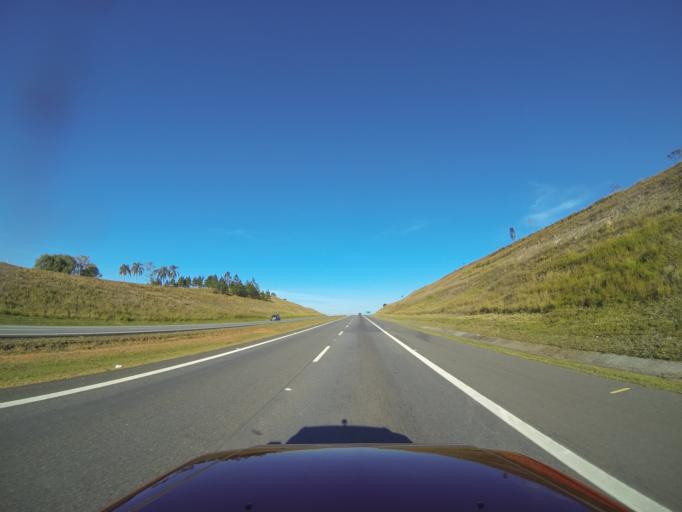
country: BR
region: Sao Paulo
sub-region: Jacarei
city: Jacarei
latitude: -23.3190
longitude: -46.0396
